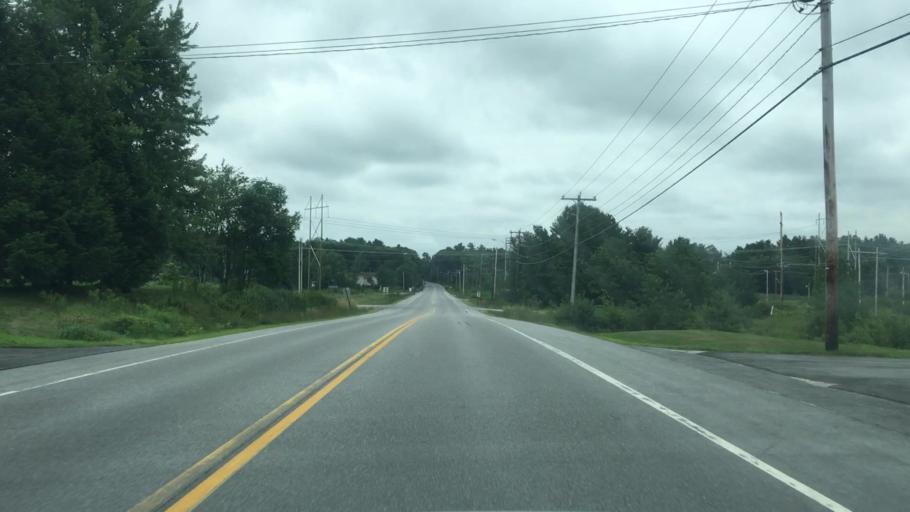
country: US
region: Maine
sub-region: York County
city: Biddeford
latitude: 43.5312
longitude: -70.5050
